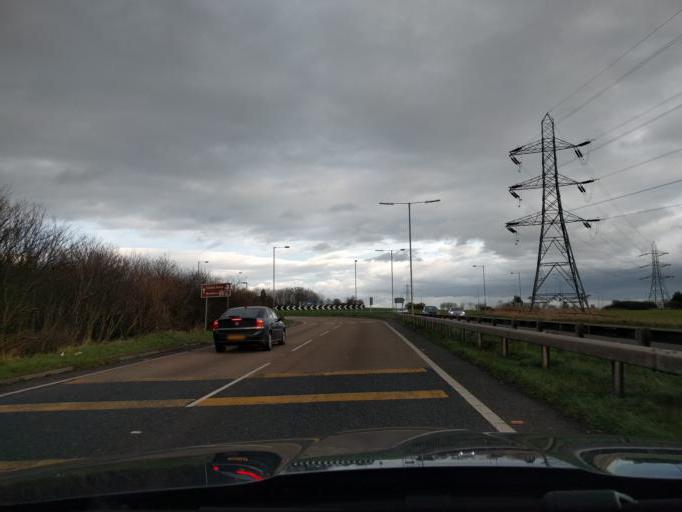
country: GB
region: England
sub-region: Northumberland
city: Newbiggin-by-the-Sea
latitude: 55.1698
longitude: -1.5330
